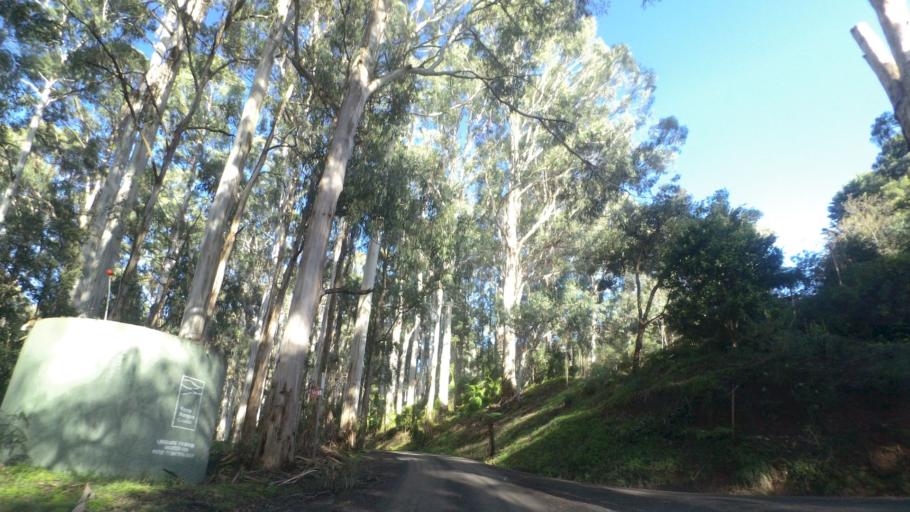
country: AU
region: Victoria
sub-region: Yarra Ranges
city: Mount Dandenong
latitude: -37.8285
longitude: 145.3728
